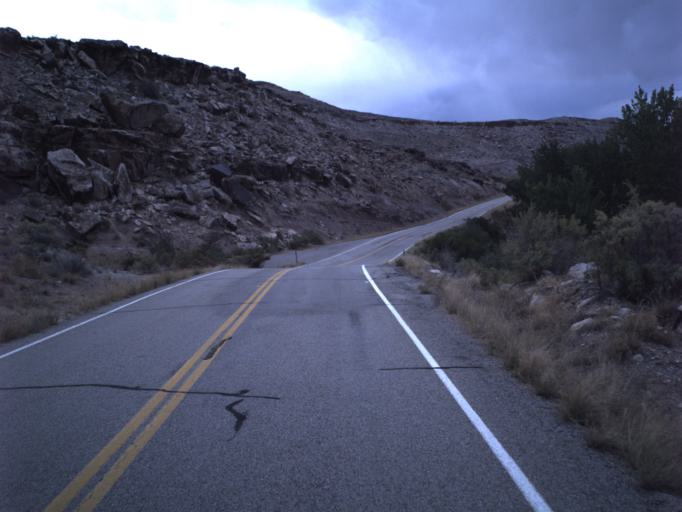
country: US
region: Utah
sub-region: Grand County
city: Moab
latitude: 38.8285
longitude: -109.2861
